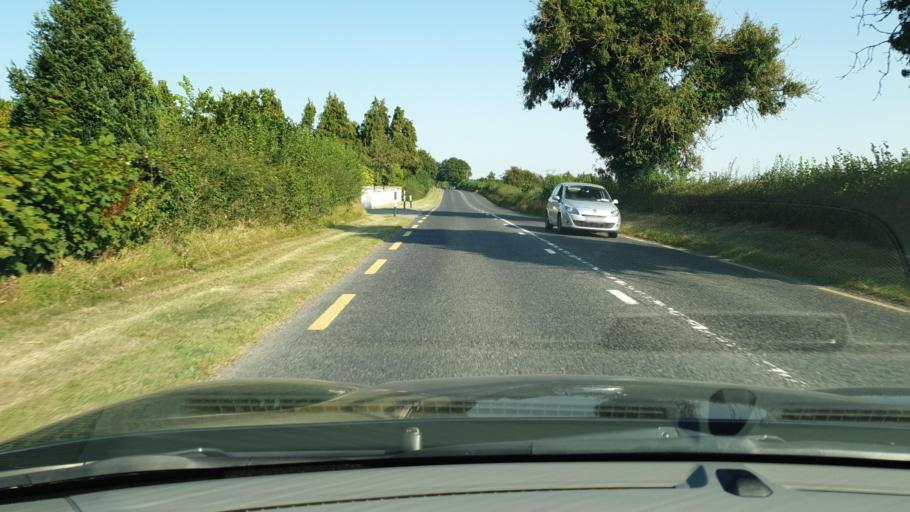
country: IE
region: Leinster
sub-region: An Mhi
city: Navan
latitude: 53.6447
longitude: -6.6341
